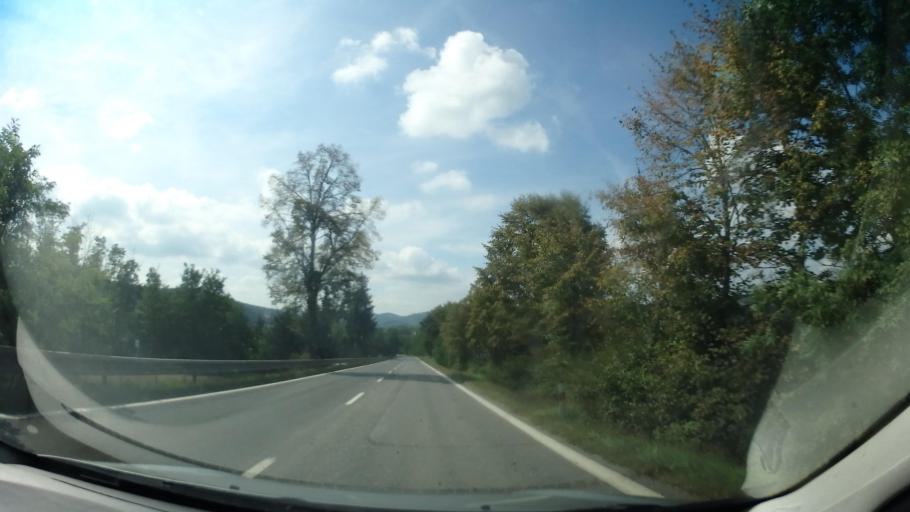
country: CZ
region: Central Bohemia
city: Krasna Hora nad Vltavou
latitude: 49.6775
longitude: 14.2967
